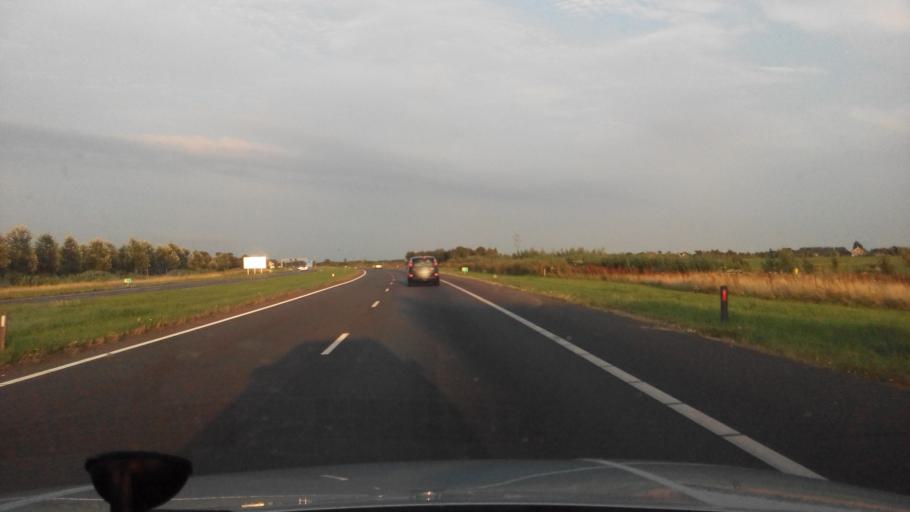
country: NL
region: South Holland
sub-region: Gemeente Alphen aan den Rijn
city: Alphen aan den Rijn
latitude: 52.1117
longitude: 4.6422
